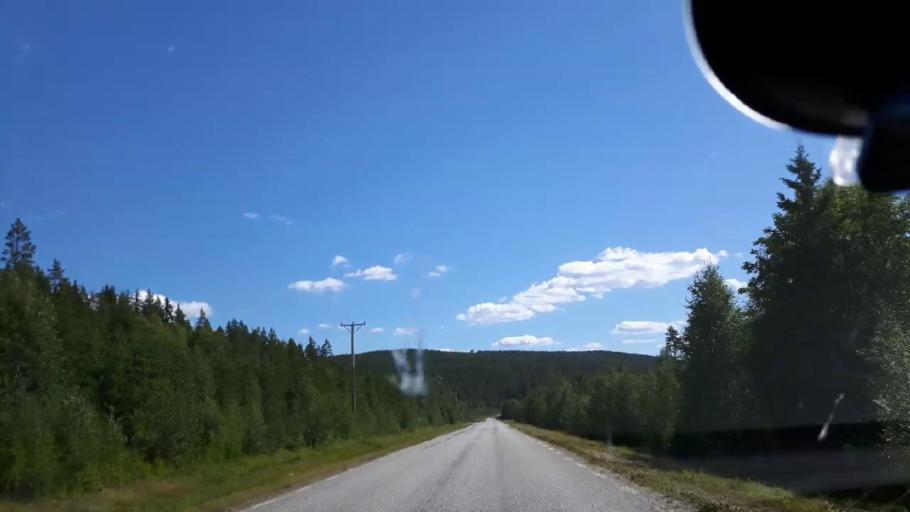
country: SE
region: Vaesternorrland
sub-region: Ange Kommun
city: Fransta
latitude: 62.7462
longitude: 16.3236
